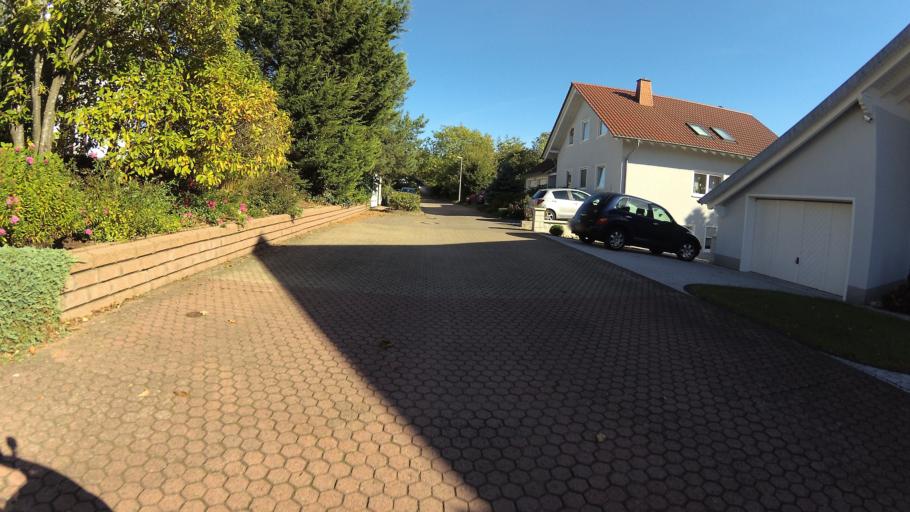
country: DE
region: Saarland
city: Eppelborn
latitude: 49.4132
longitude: 6.9599
